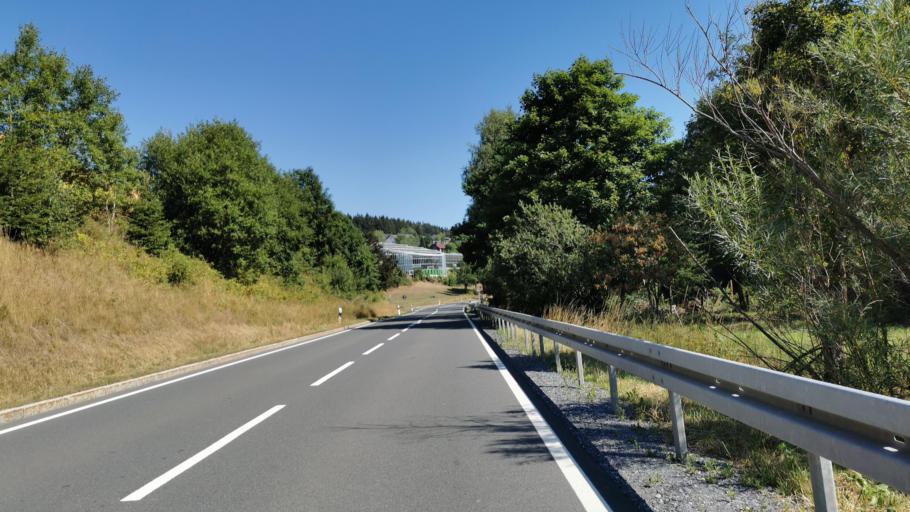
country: DE
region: Bavaria
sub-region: Upper Franconia
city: Tettau
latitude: 50.4661
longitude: 11.2752
